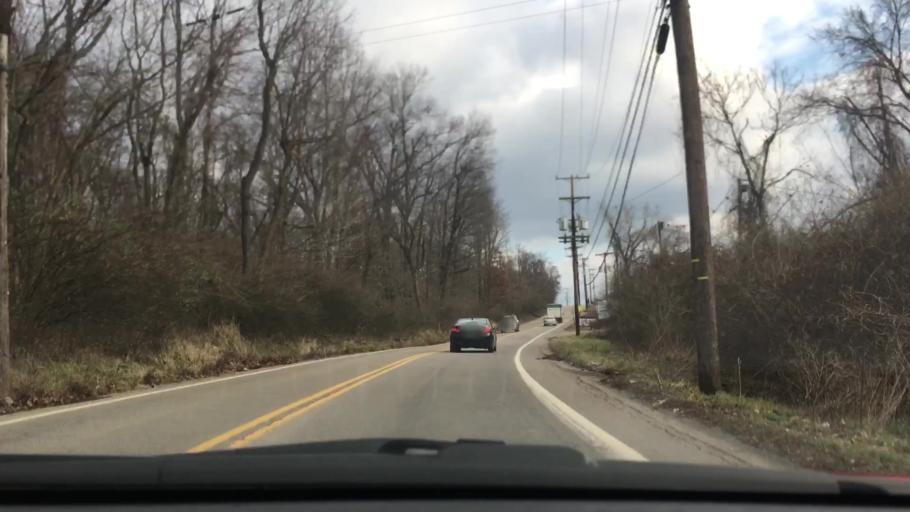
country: US
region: Pennsylvania
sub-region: Allegheny County
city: Pleasant Hills
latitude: 40.3529
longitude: -79.9541
